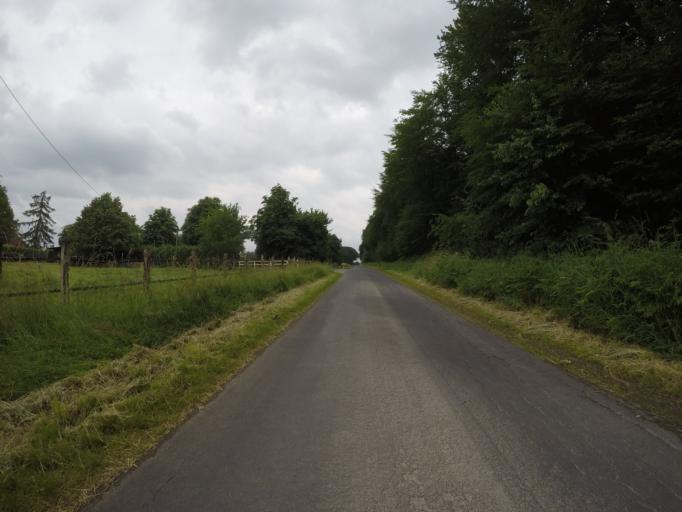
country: DE
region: North Rhine-Westphalia
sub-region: Regierungsbezirk Dusseldorf
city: Hunxe
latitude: 51.6162
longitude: 6.8324
